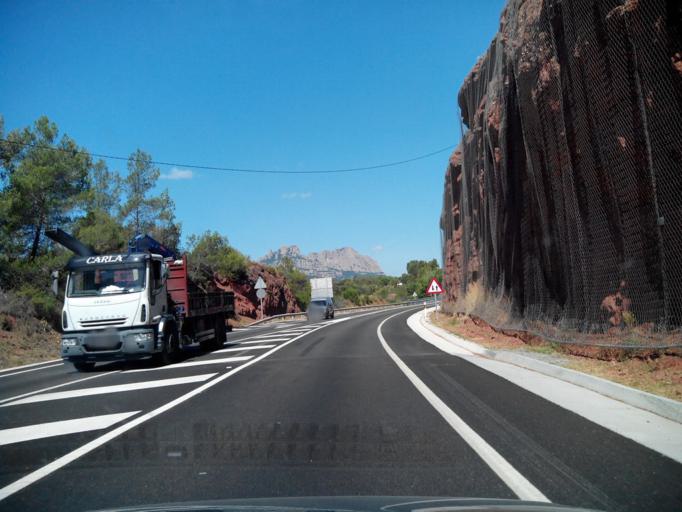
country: ES
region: Catalonia
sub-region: Provincia de Barcelona
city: Viladecavalls
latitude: 41.5863
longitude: 1.9197
